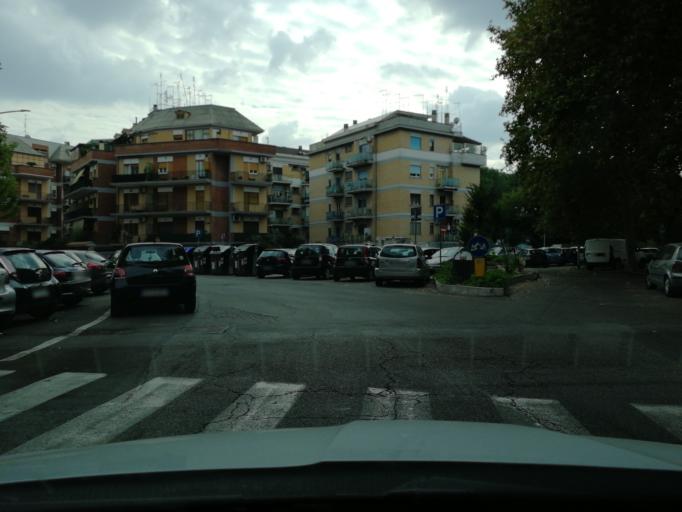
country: IT
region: Latium
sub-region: Citta metropolitana di Roma Capitale
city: Rome
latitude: 41.8626
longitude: 12.5467
